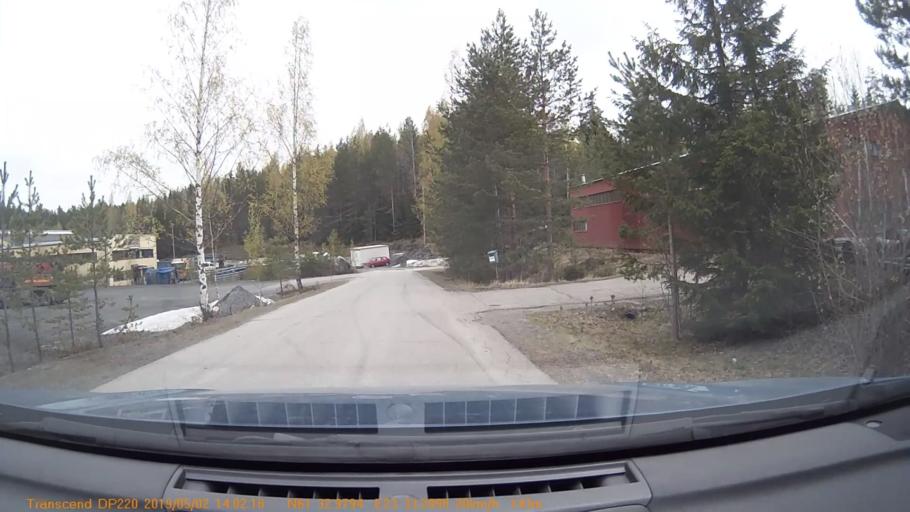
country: FI
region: Pirkanmaa
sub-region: Tampere
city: Yloejaervi
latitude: 61.5496
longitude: 23.5536
